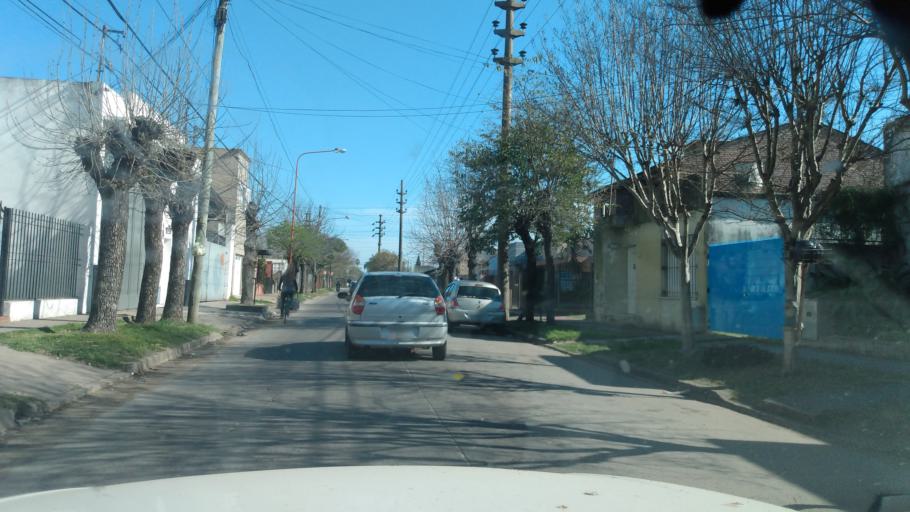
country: AR
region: Buenos Aires
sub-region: Partido de Lujan
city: Lujan
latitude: -34.5745
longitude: -59.1003
